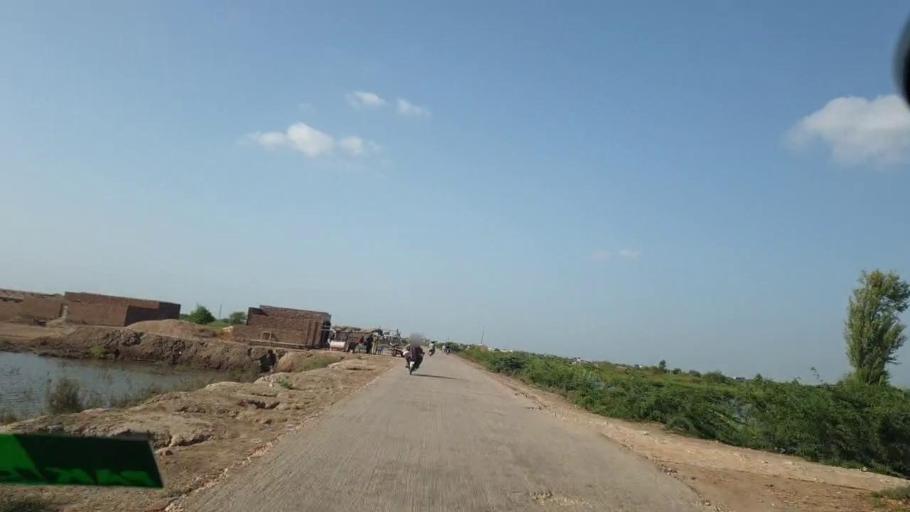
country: PK
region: Sindh
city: Naukot
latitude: 24.7464
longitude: 69.1977
